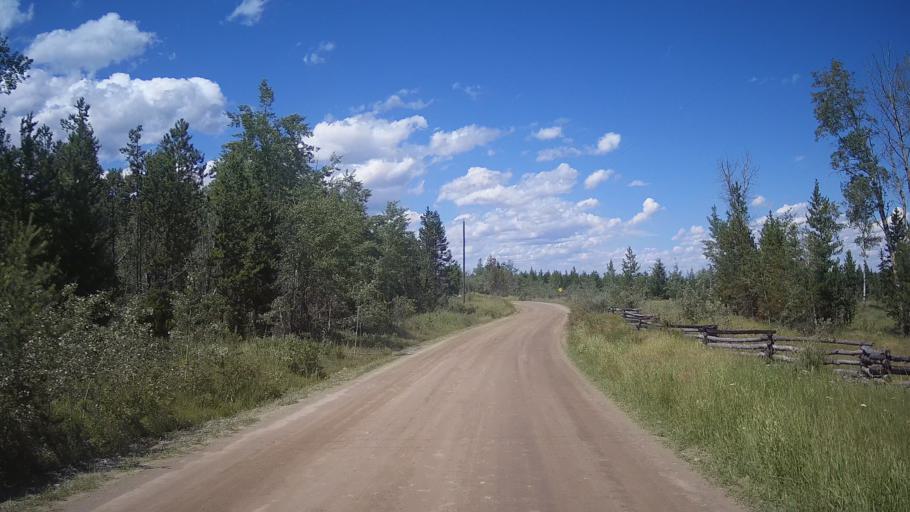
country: CA
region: British Columbia
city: Cache Creek
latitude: 51.2636
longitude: -121.6967
